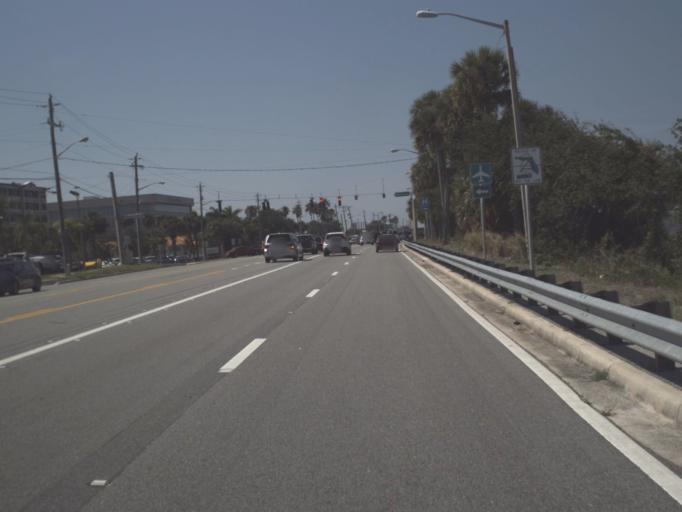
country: US
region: Florida
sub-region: Brevard County
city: Melbourne
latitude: 28.0928
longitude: -80.6095
